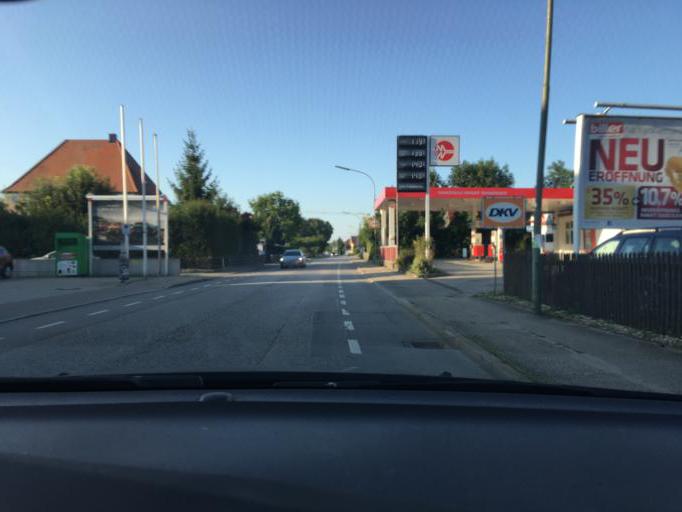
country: DE
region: Bavaria
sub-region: Upper Bavaria
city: Erding
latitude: 48.3121
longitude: 11.9200
